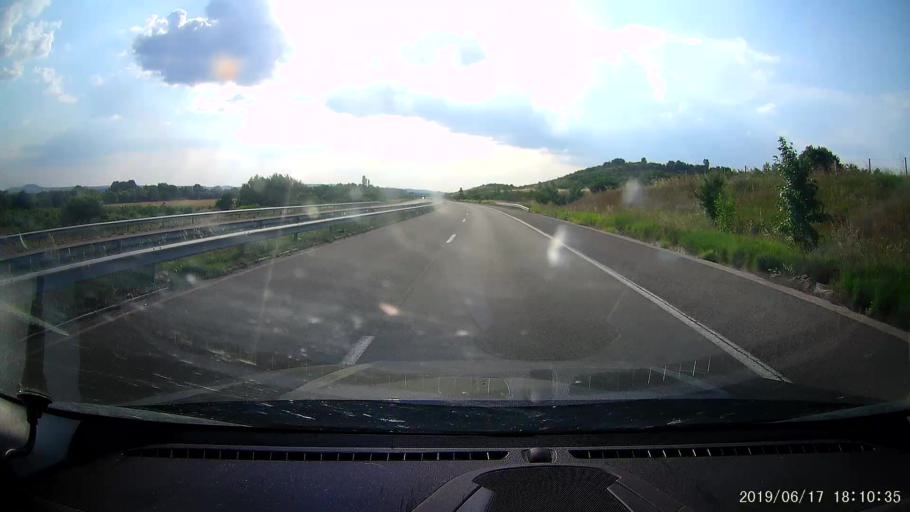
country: BG
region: Khaskovo
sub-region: Obshtina Lyubimets
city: Lyubimets
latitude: 41.8758
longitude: 26.0740
